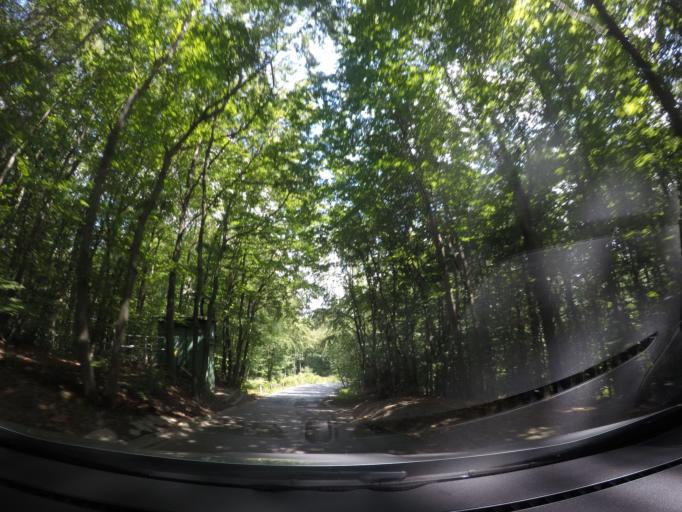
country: AT
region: Lower Austria
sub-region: Politischer Bezirk Wien-Umgebung
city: Purkersdorf
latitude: 48.2212
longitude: 16.2683
